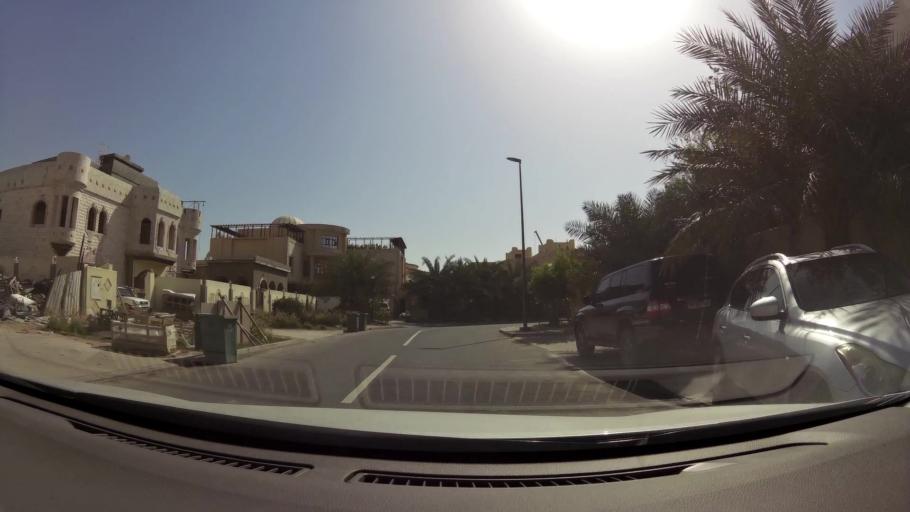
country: QA
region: Baladiyat ad Dawhah
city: Doha
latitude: 25.3638
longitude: 51.5187
